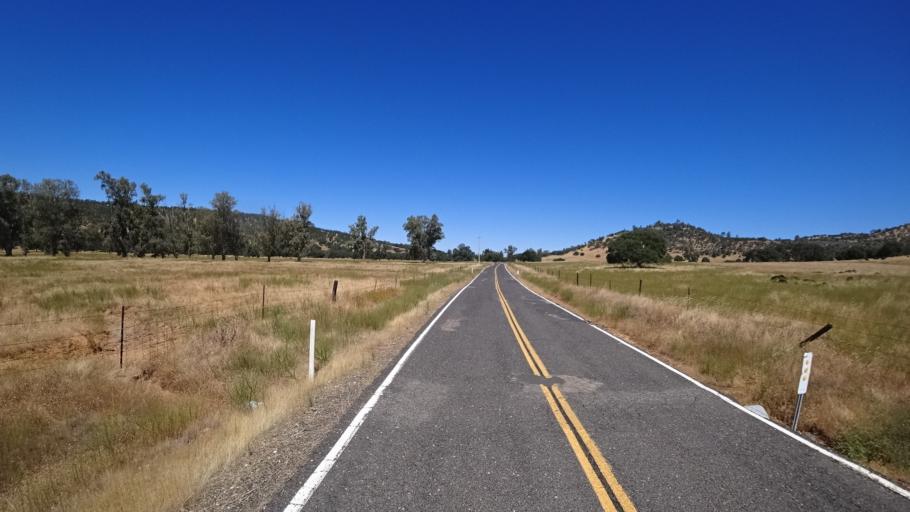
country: US
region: California
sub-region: Calaveras County
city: Copperopolis
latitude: 38.0159
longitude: -120.6759
